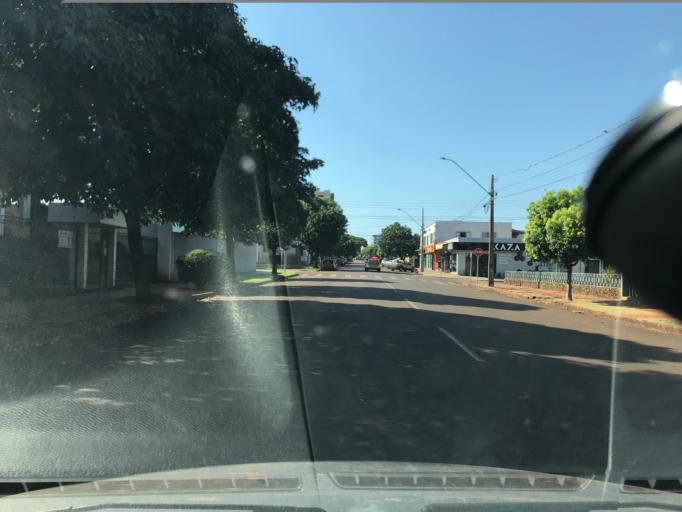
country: BR
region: Parana
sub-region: Palotina
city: Palotina
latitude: -24.2808
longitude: -53.8421
